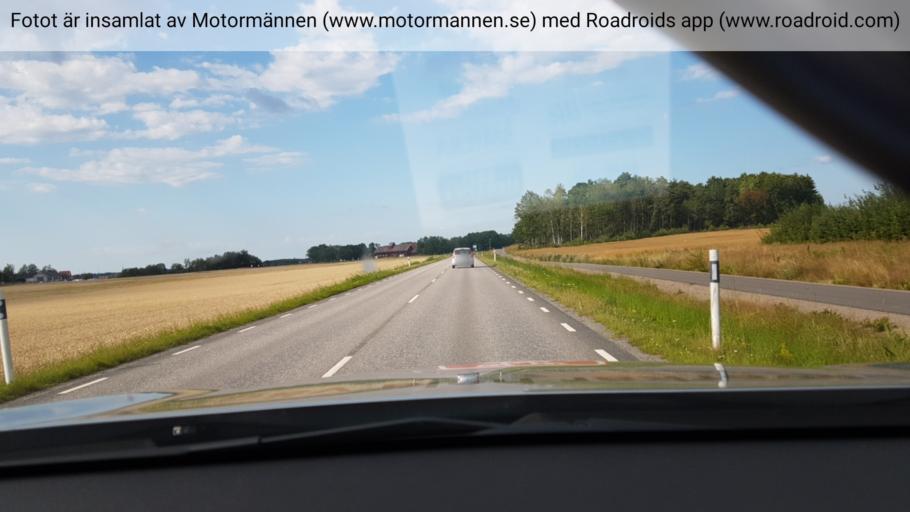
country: SE
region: Vaestra Goetaland
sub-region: Lidkopings Kommun
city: Lidkoping
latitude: 58.5510
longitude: 13.1155
